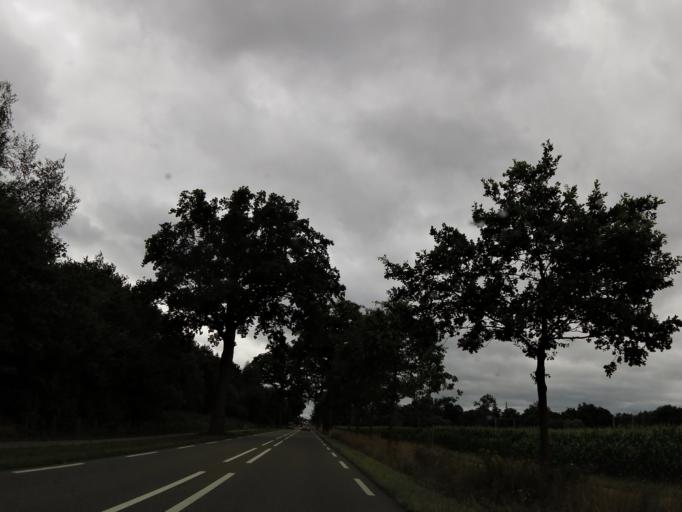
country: NL
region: Limburg
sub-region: Gemeente Maasgouw
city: Maasbracht
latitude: 51.0836
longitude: 5.8741
